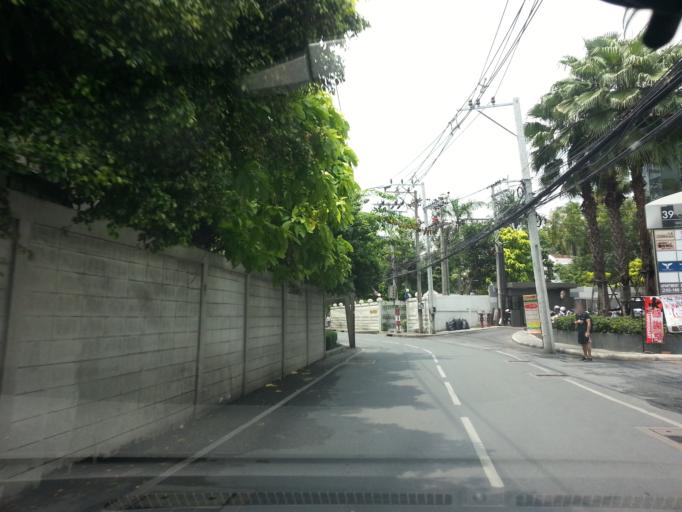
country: TH
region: Bangkok
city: Watthana
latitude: 13.7373
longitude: 100.5700
